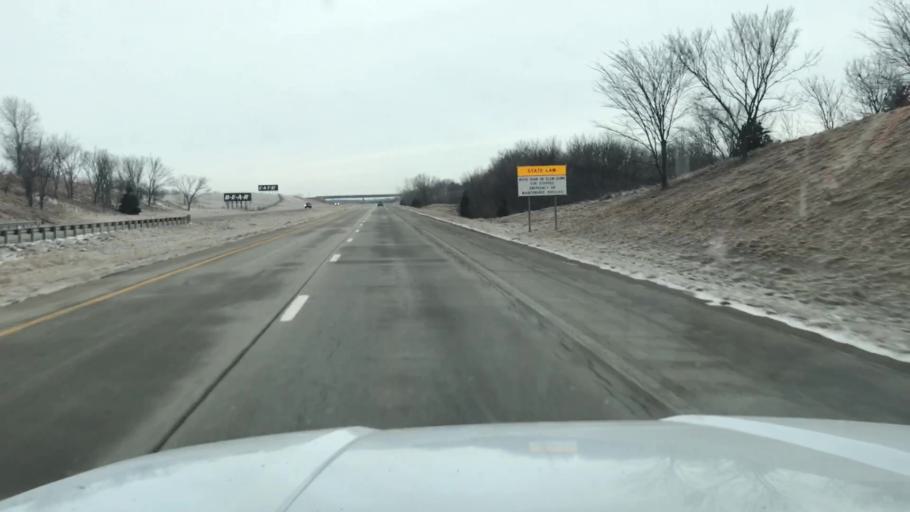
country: US
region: Missouri
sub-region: Andrew County
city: Savannah
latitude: 39.8921
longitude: -94.8570
